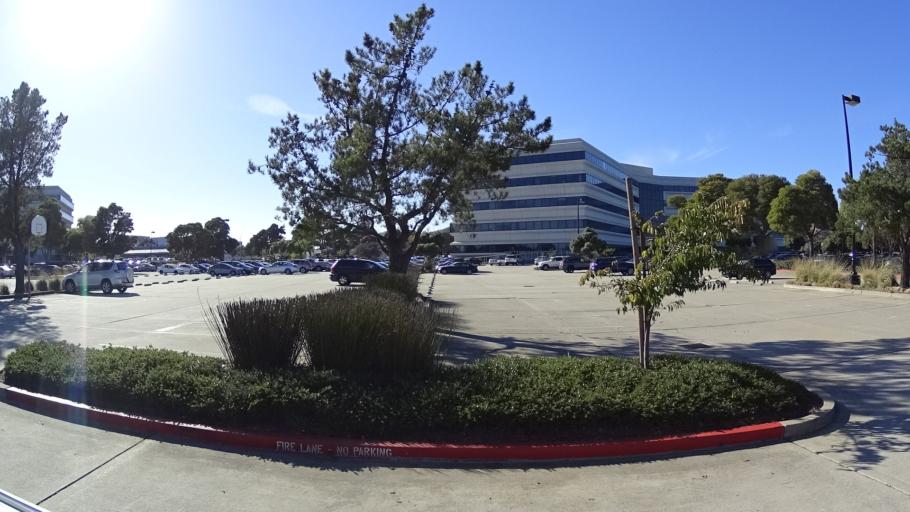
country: US
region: California
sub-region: San Mateo County
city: Brisbane
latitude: 37.6669
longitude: -122.3814
